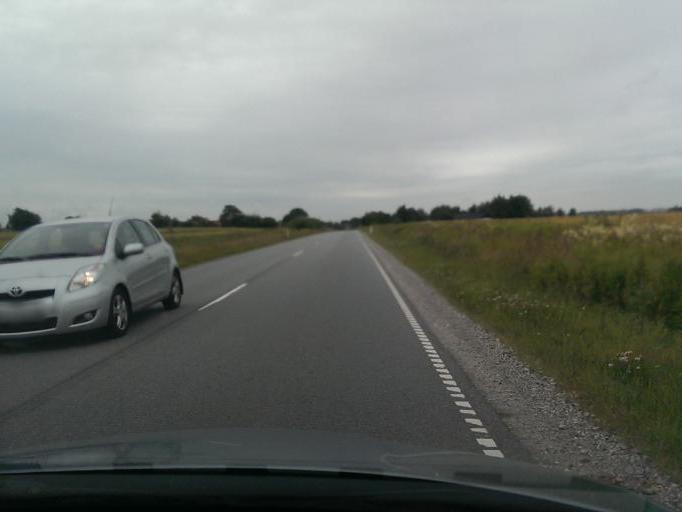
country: DK
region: North Denmark
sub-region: Hjorring Kommune
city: Vra
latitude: 57.3567
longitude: 9.9233
